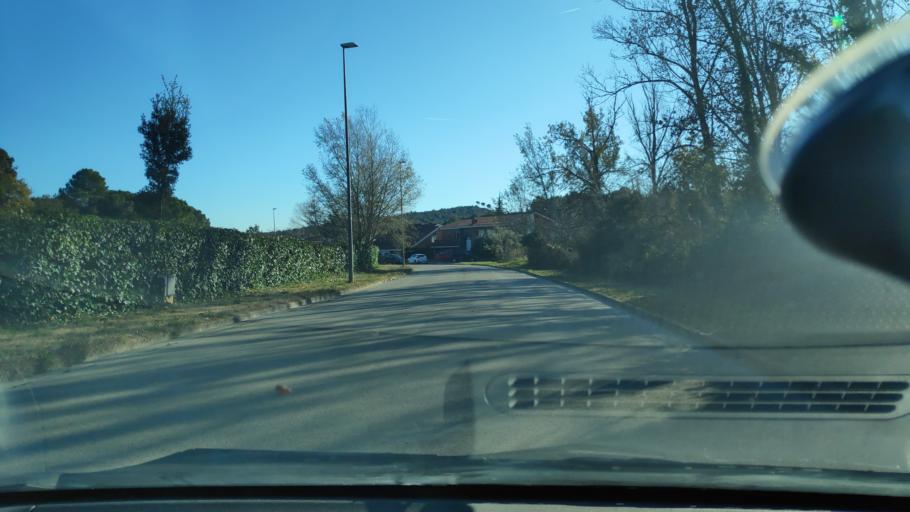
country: ES
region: Catalonia
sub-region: Provincia de Barcelona
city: Sant Quirze del Valles
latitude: 41.5377
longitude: 2.0627
